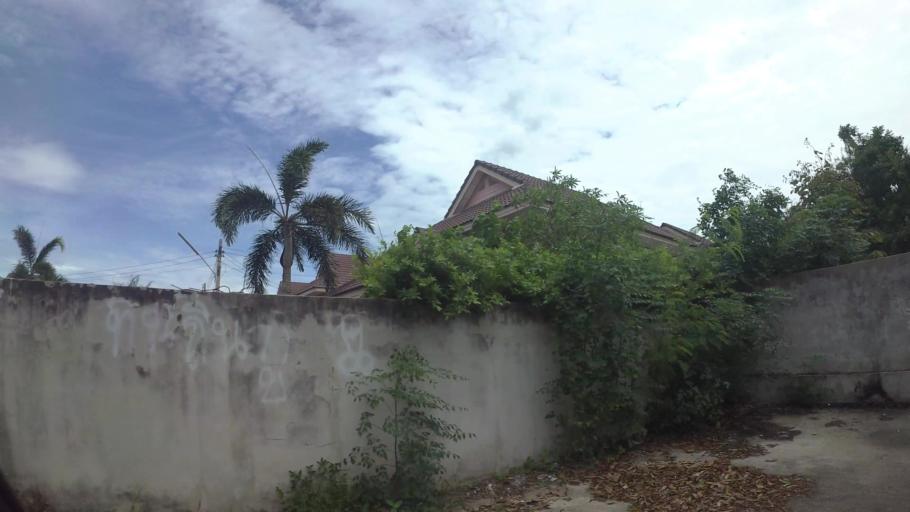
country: TH
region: Rayong
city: Rayong
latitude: 12.6818
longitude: 101.2770
